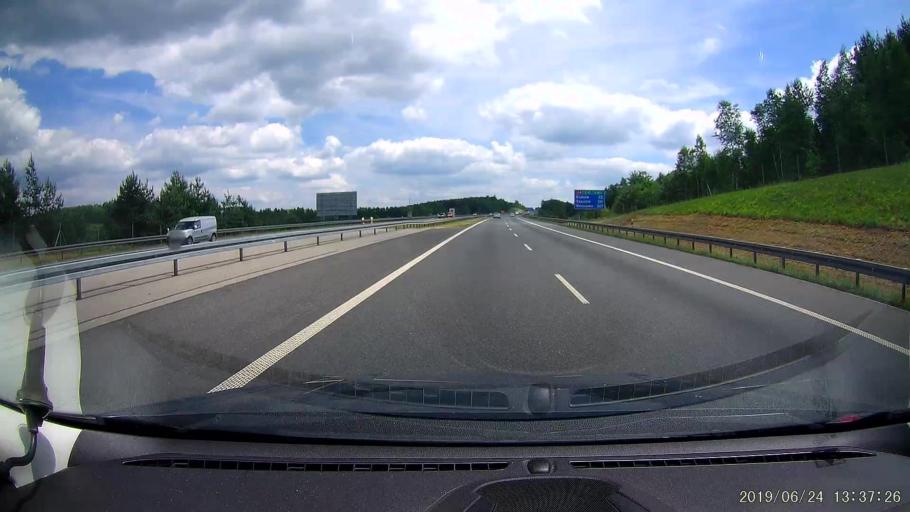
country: PL
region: Lesser Poland Voivodeship
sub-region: Powiat chrzanowski
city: Balin
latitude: 50.1537
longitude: 19.3564
